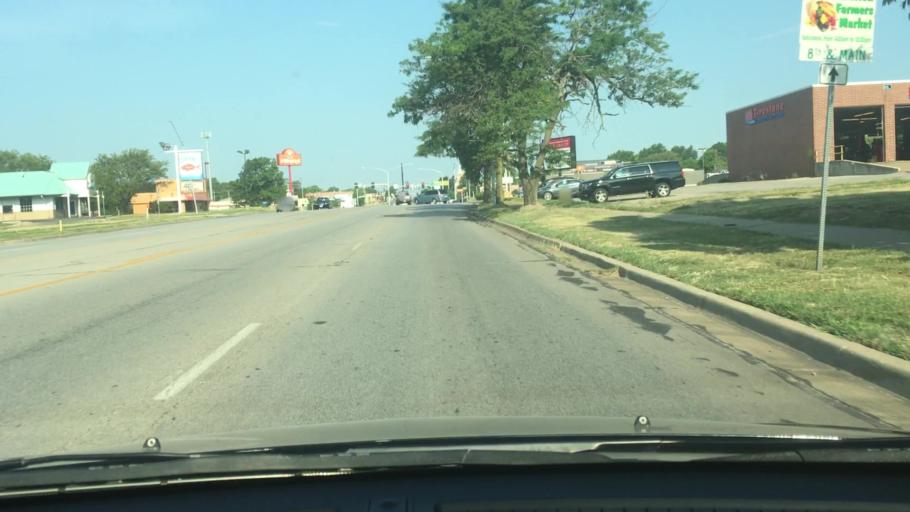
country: US
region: Missouri
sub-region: Jackson County
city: Grandview
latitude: 38.8888
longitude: -94.5220
